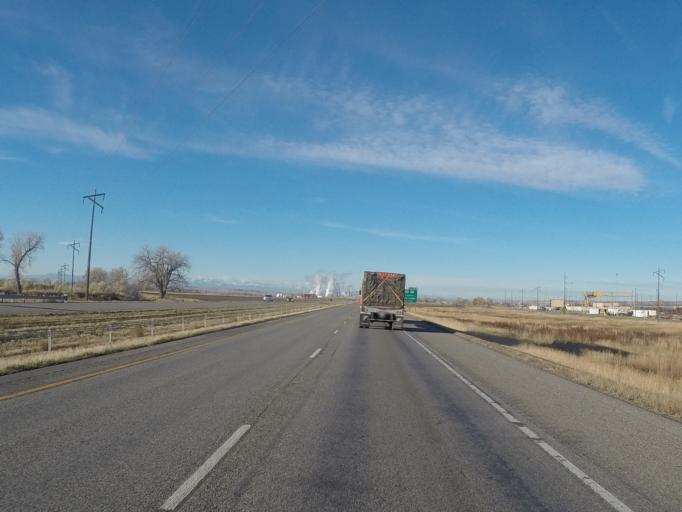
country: US
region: Montana
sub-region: Yellowstone County
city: Laurel
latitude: 45.6768
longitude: -108.7245
